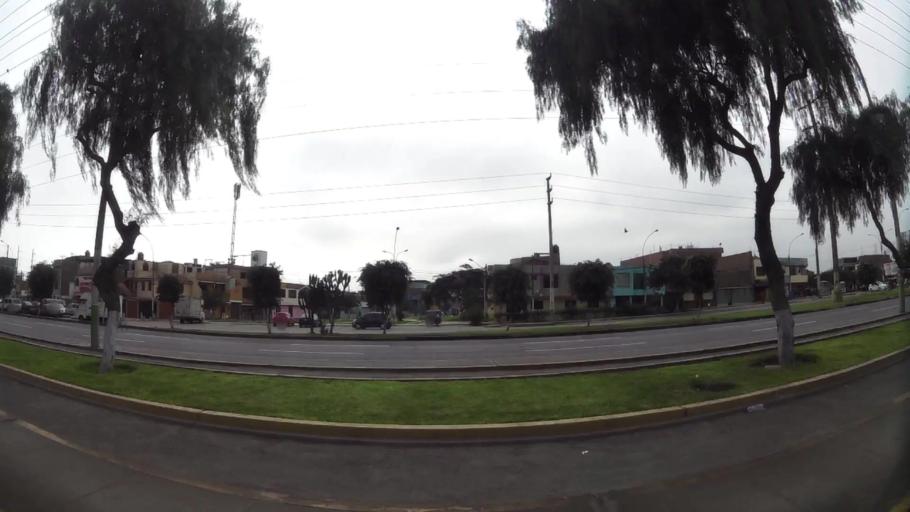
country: PE
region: Callao
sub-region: Callao
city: Callao
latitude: -12.0139
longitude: -77.0955
